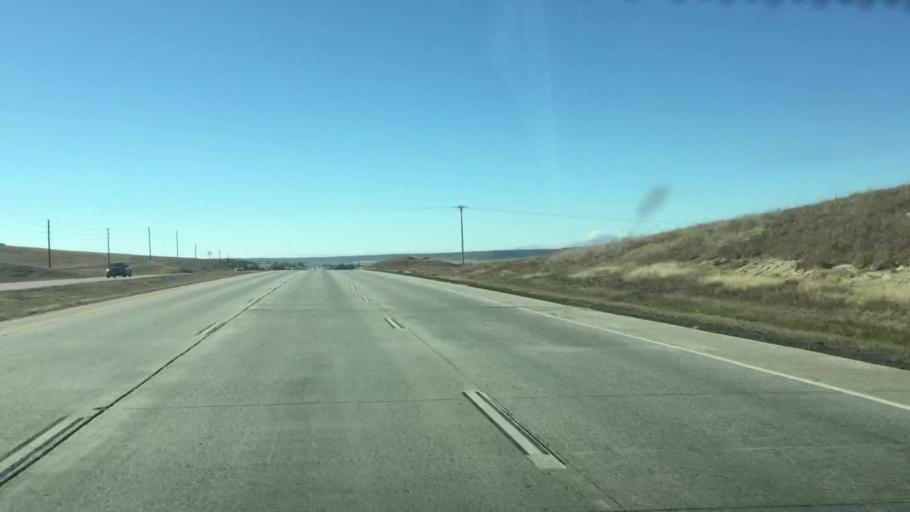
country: US
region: Colorado
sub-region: Douglas County
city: The Pinery
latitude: 39.4688
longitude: -104.7587
